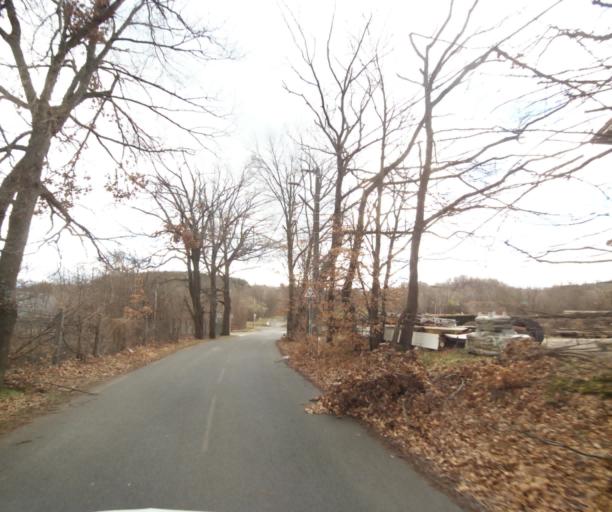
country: FR
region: Rhone-Alpes
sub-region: Departement de la Loire
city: Sorbiers
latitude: 45.4774
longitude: 4.4469
